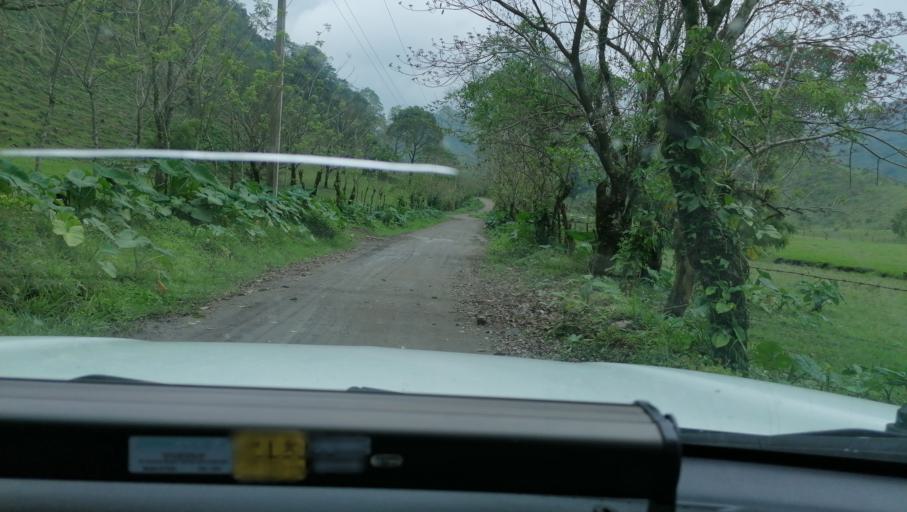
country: MX
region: Chiapas
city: Ixtacomitan
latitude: 17.3565
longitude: -93.1663
